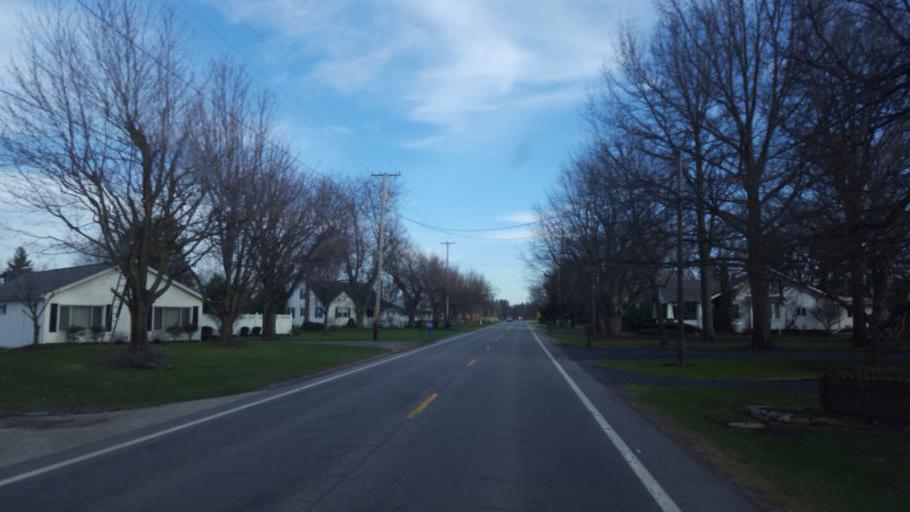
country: US
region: Ohio
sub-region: Crawford County
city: Bucyrus
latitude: 40.7854
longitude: -82.9431
